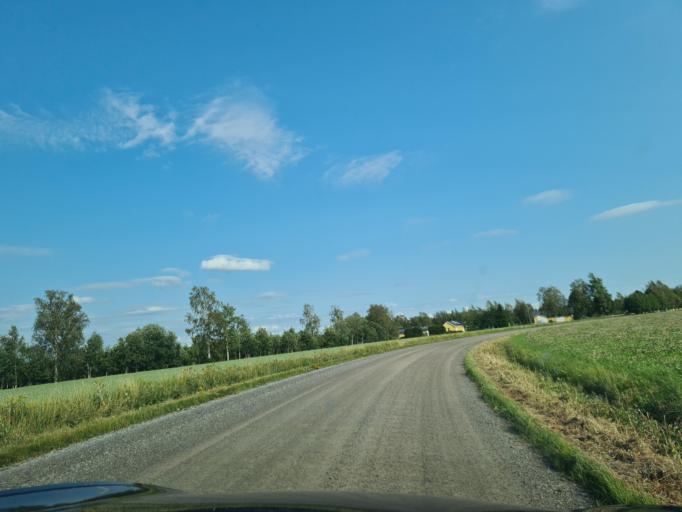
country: FI
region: Ostrobothnia
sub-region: Kyroenmaa
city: Laihia
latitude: 63.0300
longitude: 21.8929
